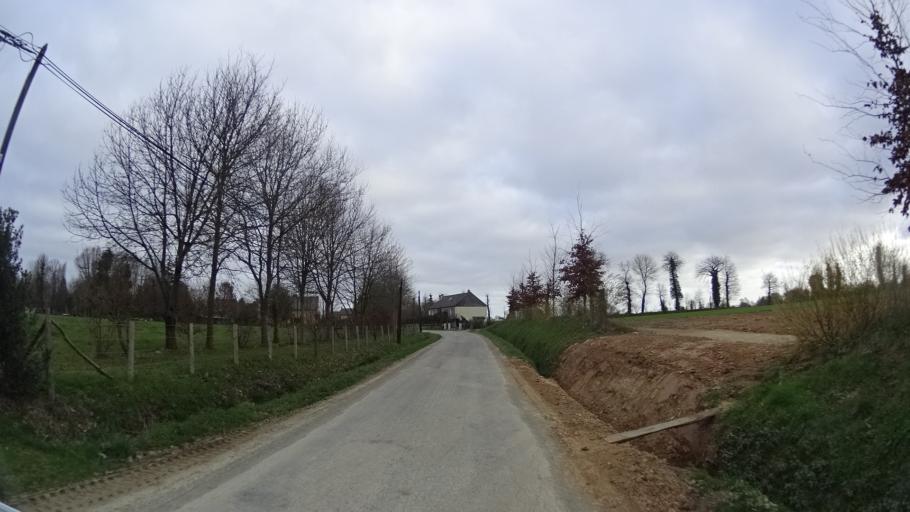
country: FR
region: Brittany
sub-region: Departement d'Ille-et-Vilaine
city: Saint-Gilles
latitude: 48.1795
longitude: -1.8602
